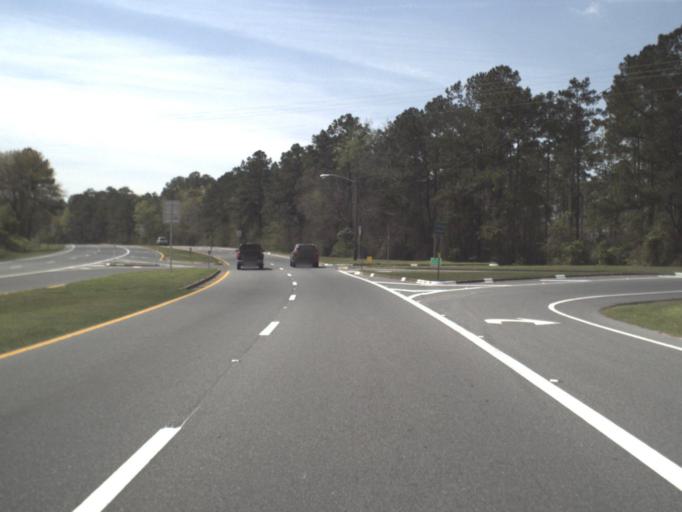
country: US
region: Florida
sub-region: Gadsden County
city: Havana
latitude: 30.6150
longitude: -84.4211
